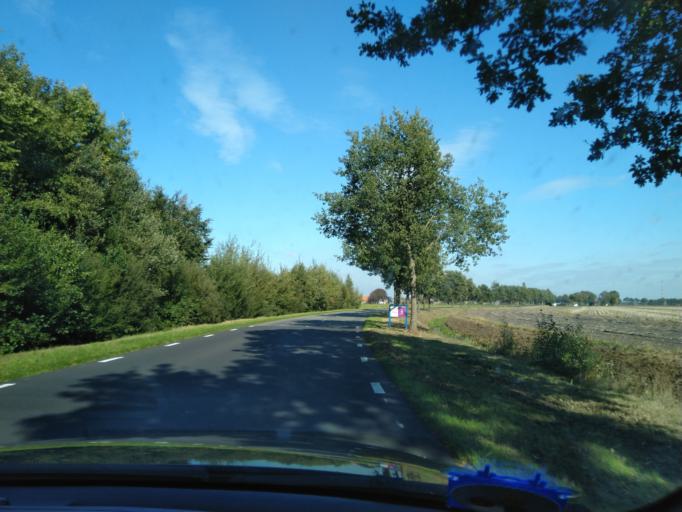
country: NL
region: Groningen
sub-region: Gemeente Hoogezand-Sappemeer
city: Sappemeer
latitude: 53.0864
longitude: 6.7892
